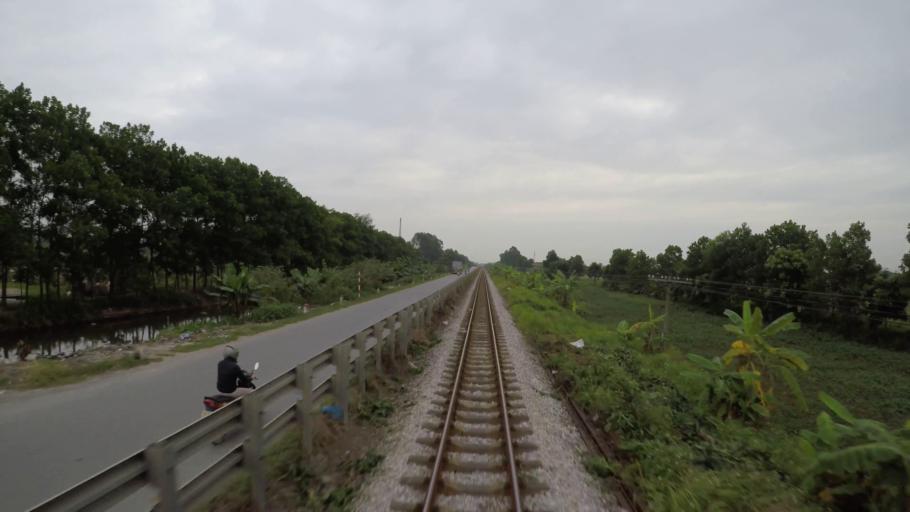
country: VN
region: Hung Yen
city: Ban Yen Nhan
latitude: 20.9853
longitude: 106.0648
